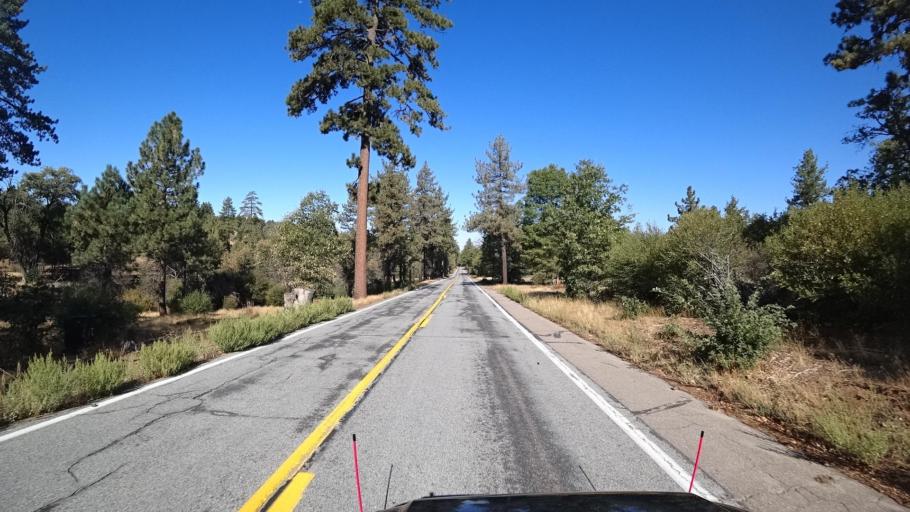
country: US
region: California
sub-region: San Diego County
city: Pine Valley
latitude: 32.8846
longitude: -116.4311
